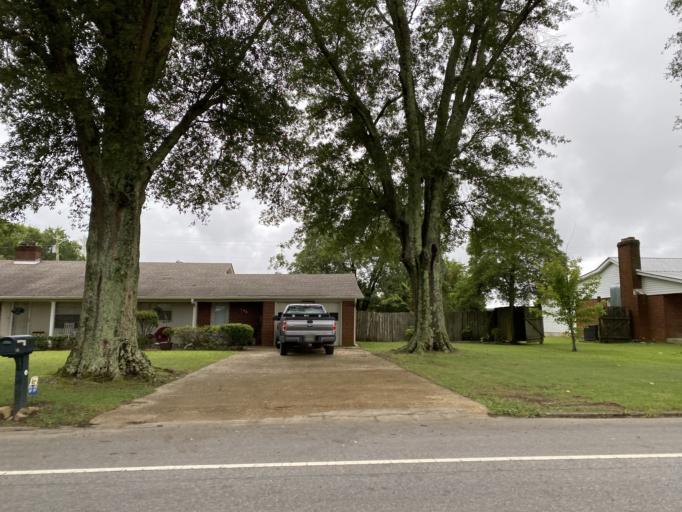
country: US
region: Alabama
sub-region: Franklin County
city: Red Bay
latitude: 34.4427
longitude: -88.1532
